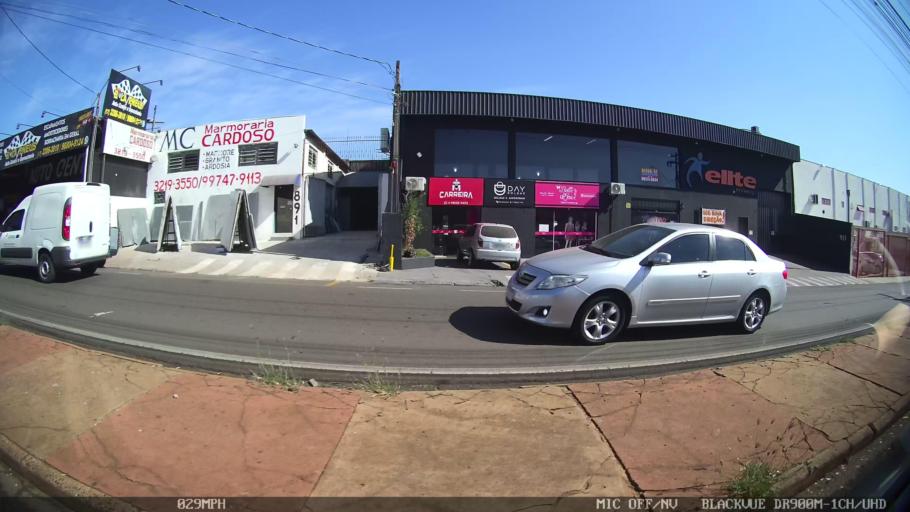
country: BR
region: Sao Paulo
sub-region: Sao Jose Do Rio Preto
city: Sao Jose do Rio Preto
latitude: -20.7807
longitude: -49.3866
